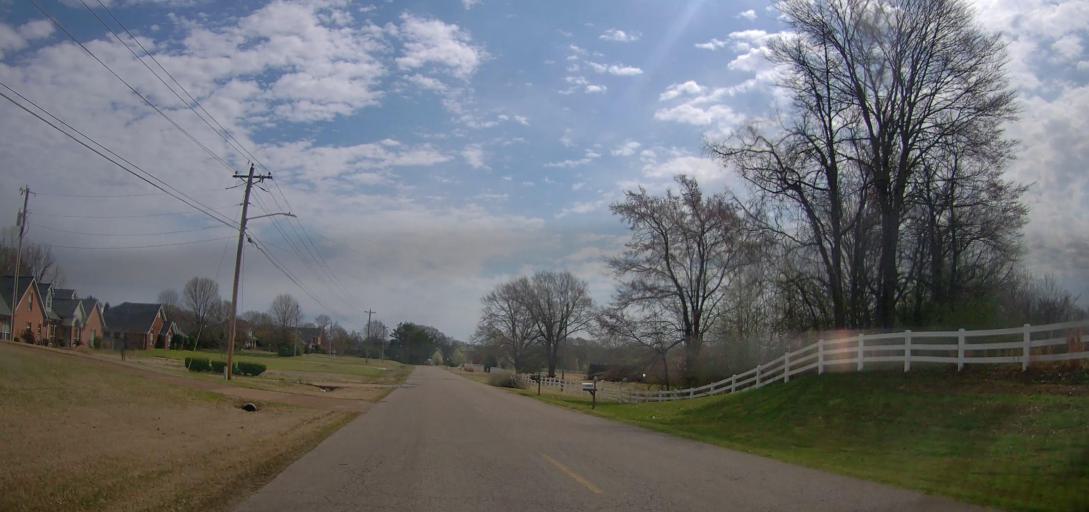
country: US
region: Mississippi
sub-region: De Soto County
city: Olive Branch
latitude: 34.9913
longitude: -89.8518
